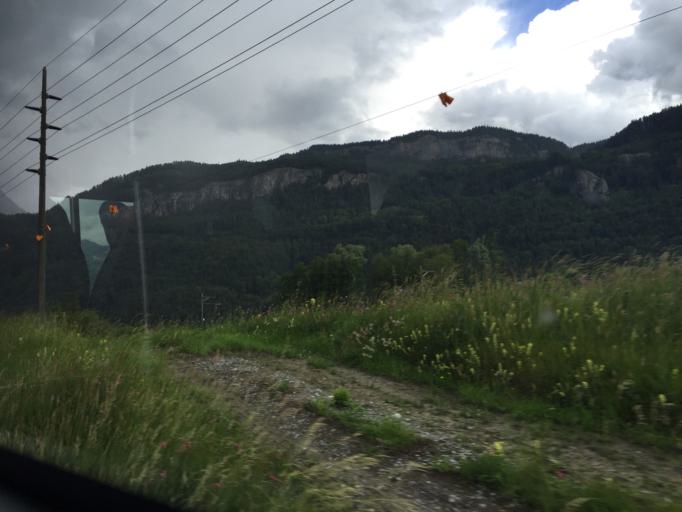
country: CH
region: Bern
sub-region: Interlaken-Oberhasli District
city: Meiringen
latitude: 46.7367
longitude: 8.1544
